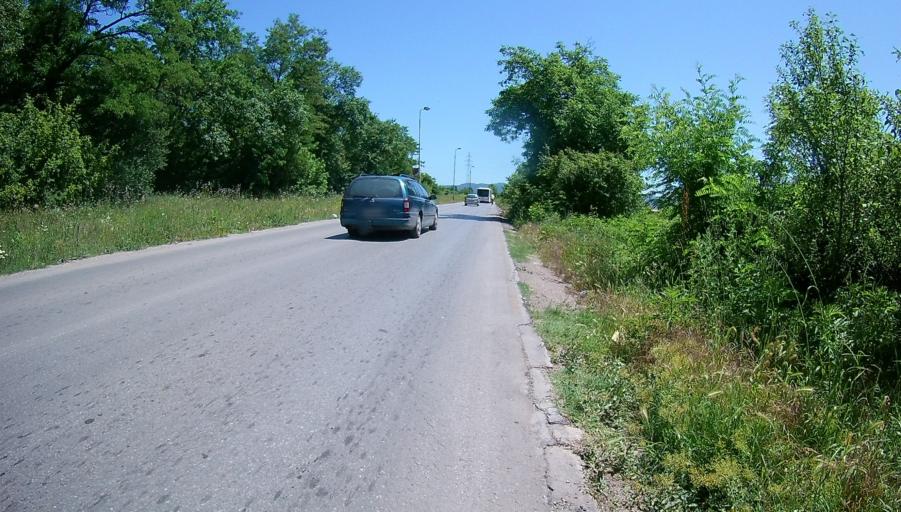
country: RS
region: Central Serbia
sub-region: Nisavski Okrug
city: Nis
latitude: 43.2990
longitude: 21.8768
